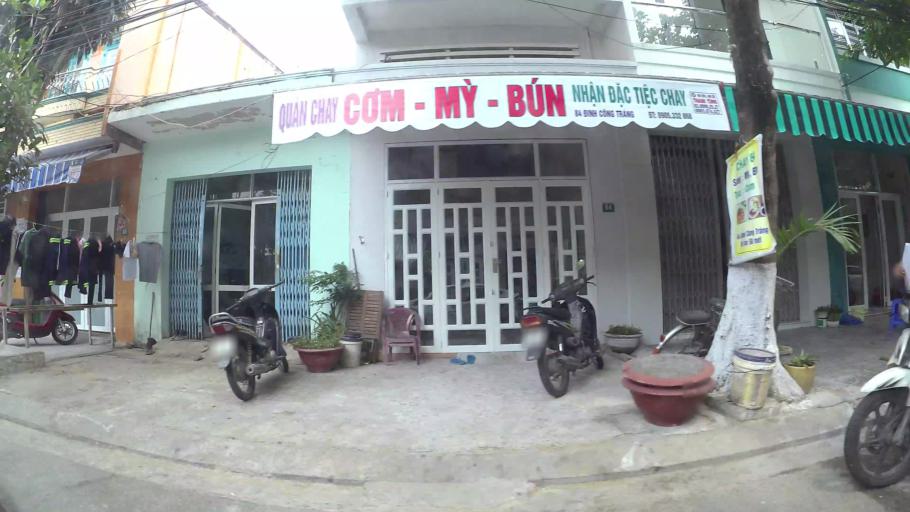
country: VN
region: Da Nang
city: Da Nang
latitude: 16.0888
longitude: 108.2178
